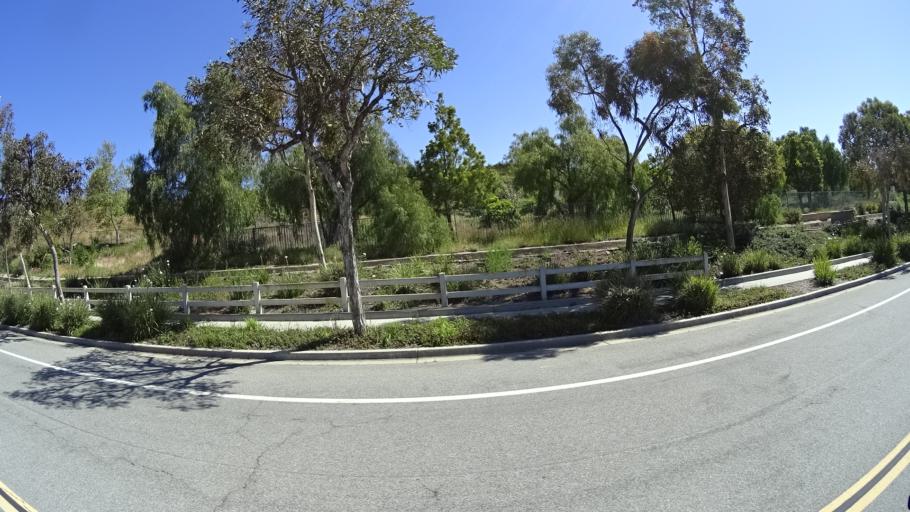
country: US
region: California
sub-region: Ventura County
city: Casa Conejo
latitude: 34.1595
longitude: -118.9866
